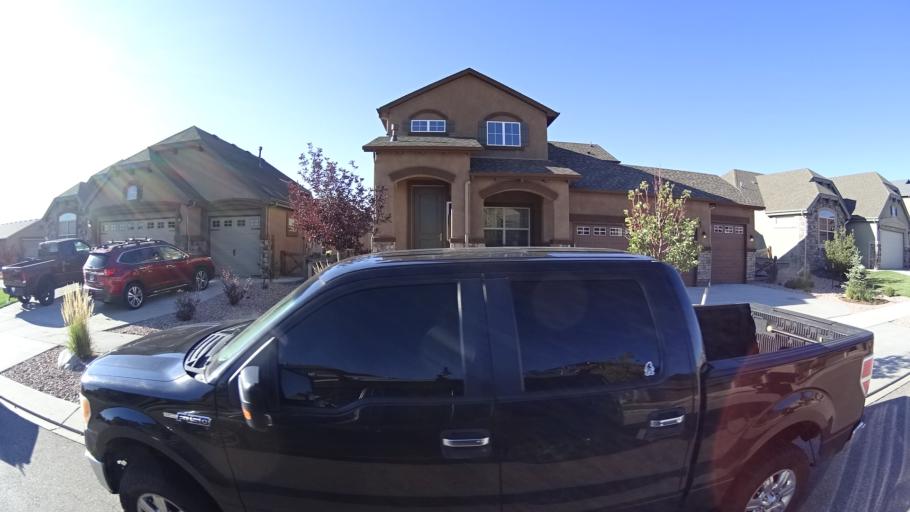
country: US
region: Colorado
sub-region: El Paso County
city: Black Forest
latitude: 38.9367
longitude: -104.6680
